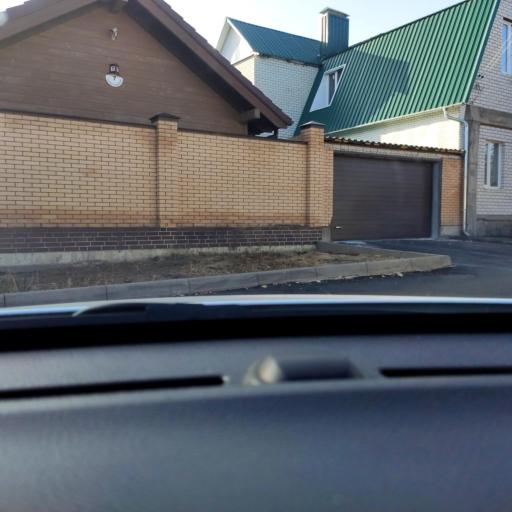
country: RU
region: Voronezj
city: Voronezh
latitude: 51.6973
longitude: 39.2120
